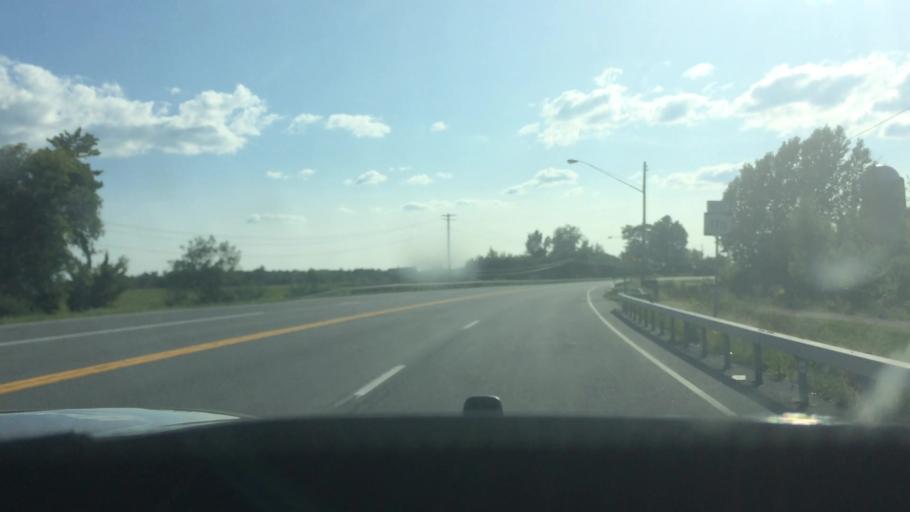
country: US
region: New York
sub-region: St. Lawrence County
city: Hannawa Falls
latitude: 44.6942
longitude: -74.6641
